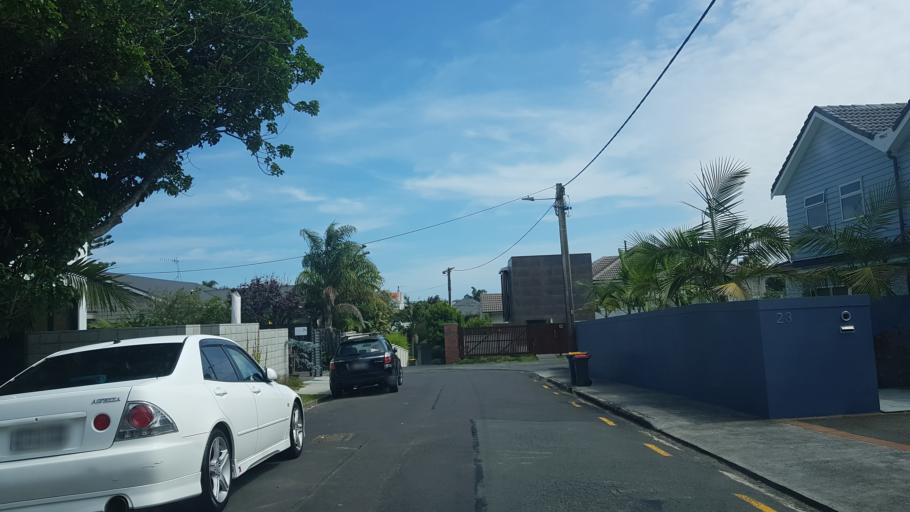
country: NZ
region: Auckland
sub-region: Auckland
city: North Shore
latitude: -36.7923
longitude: 174.7782
